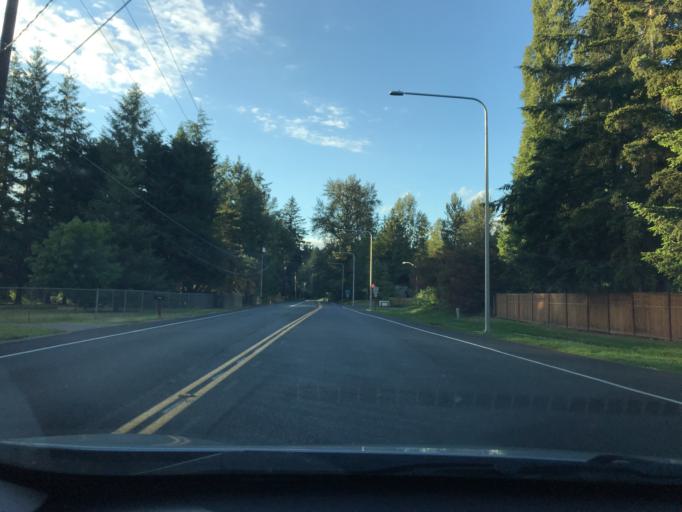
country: US
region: Washington
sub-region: King County
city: Lake Morton-Berrydale
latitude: 47.3024
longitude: -122.0866
